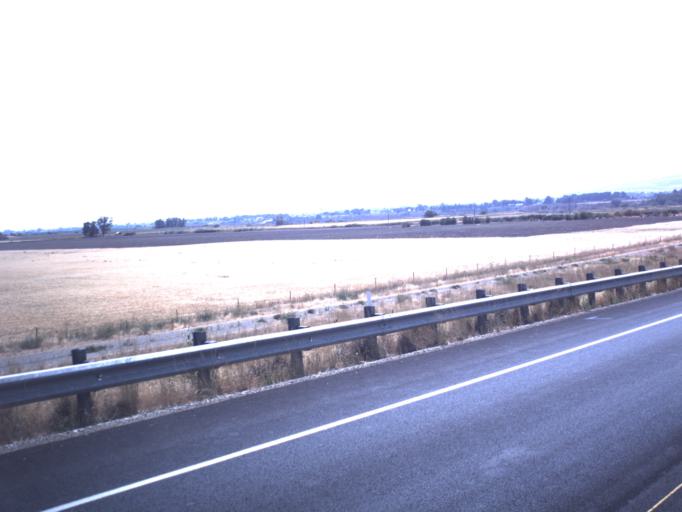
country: US
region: Utah
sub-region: Box Elder County
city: Garland
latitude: 41.7845
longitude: -112.0971
